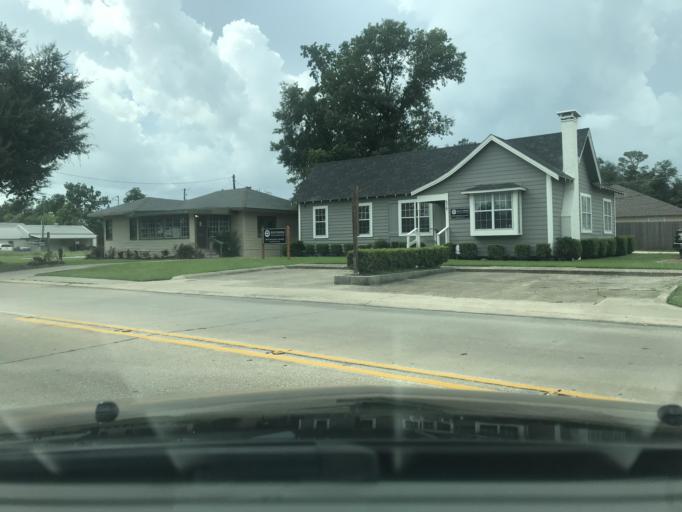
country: US
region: Louisiana
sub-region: Calcasieu Parish
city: Lake Charles
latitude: 30.2033
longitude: -93.2150
